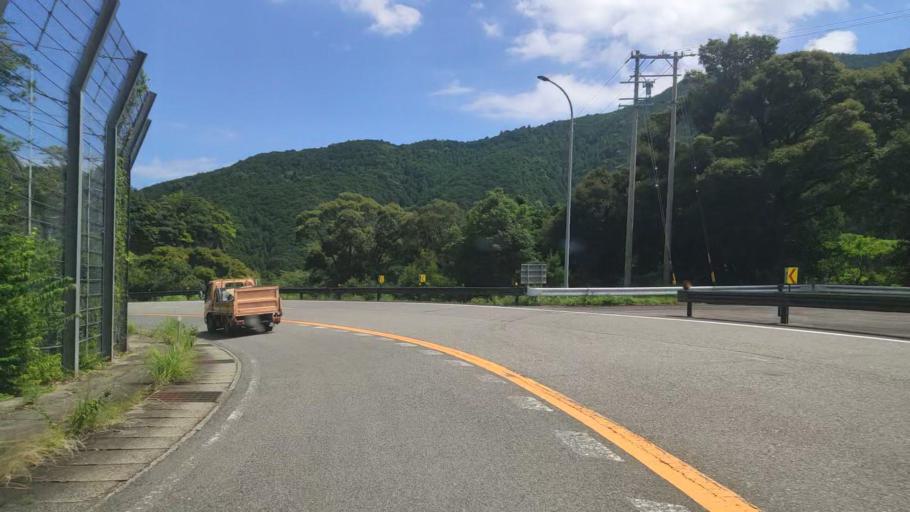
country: JP
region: Mie
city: Owase
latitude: 33.9208
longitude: 136.1013
